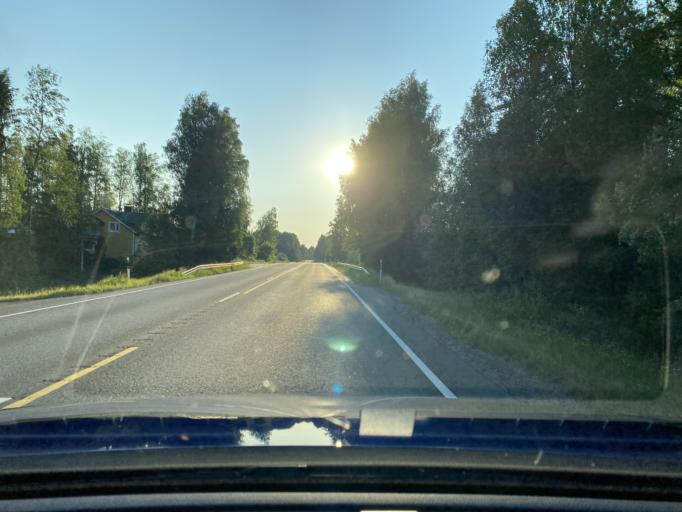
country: FI
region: Haeme
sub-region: Haemeenlinna
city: Renko
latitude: 60.7892
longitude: 24.1274
